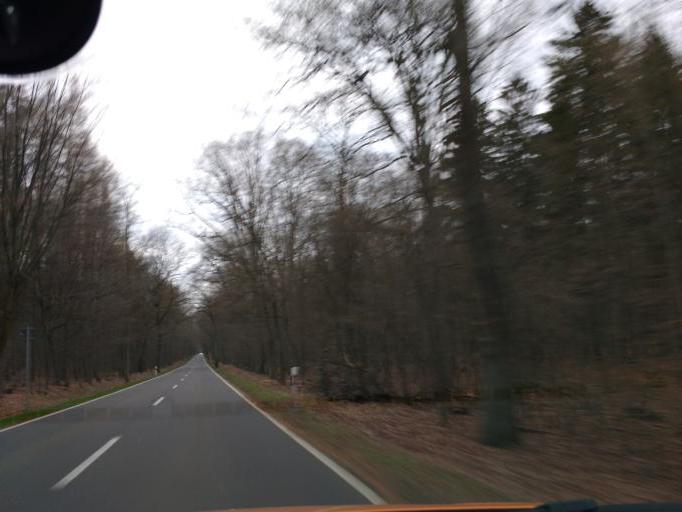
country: DE
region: Brandenburg
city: Werftpfuhl
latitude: 52.6626
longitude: 13.8298
